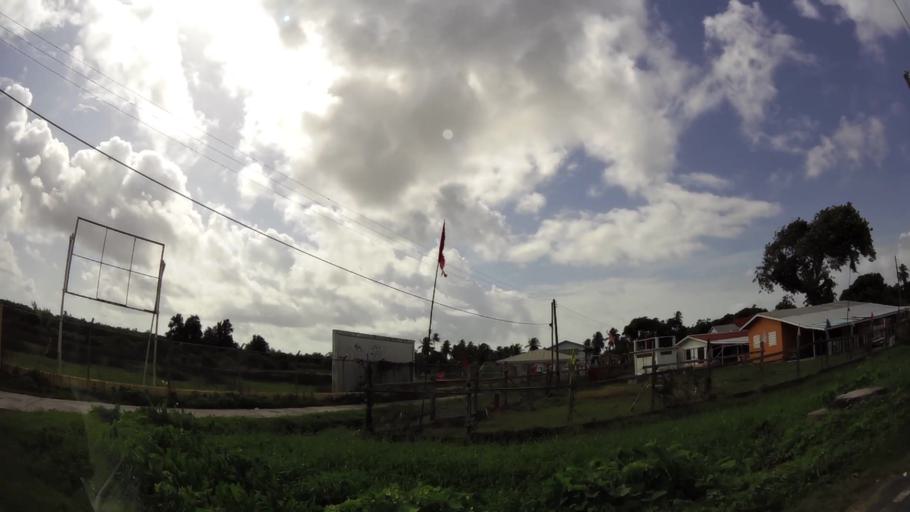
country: GY
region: Demerara-Mahaica
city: Mahaica Village
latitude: 6.7141
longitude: -57.9303
